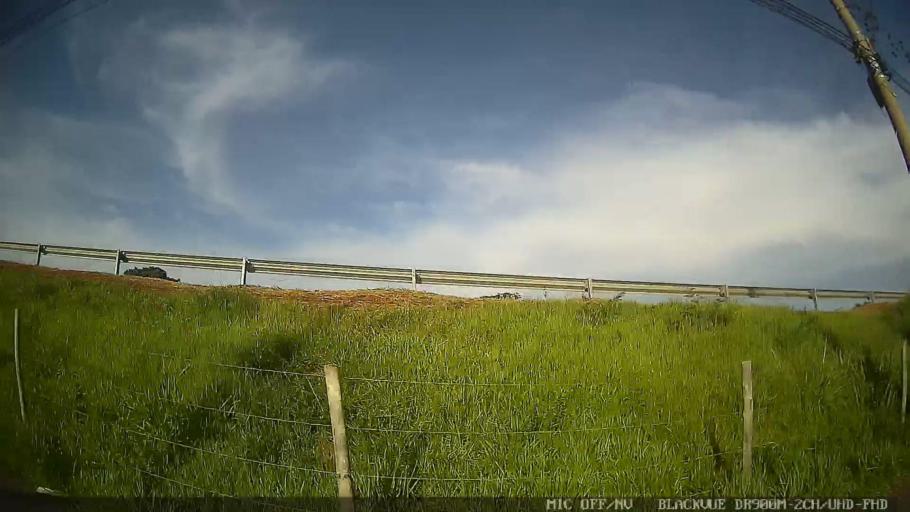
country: BR
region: Sao Paulo
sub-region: Tiete
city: Tiete
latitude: -23.0719
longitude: -47.7283
